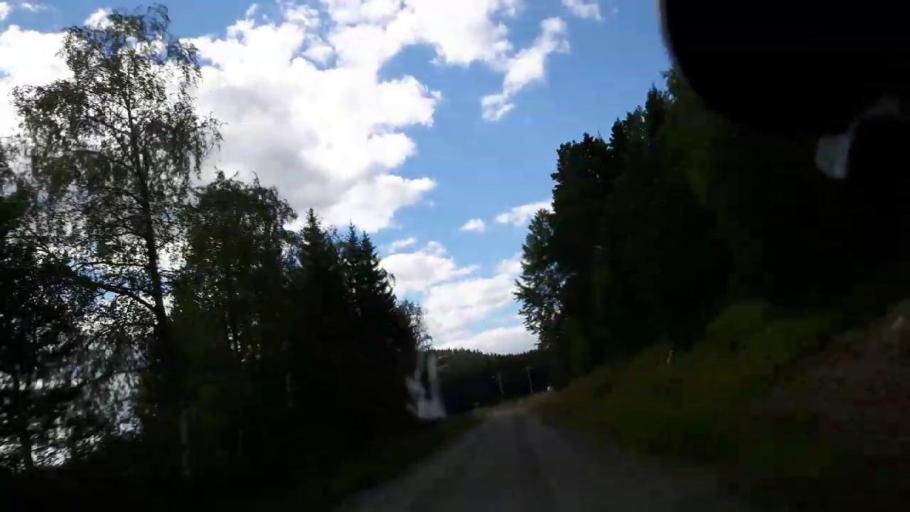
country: SE
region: Jaemtland
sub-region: Braecke Kommun
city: Braecke
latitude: 62.7192
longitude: 15.5858
